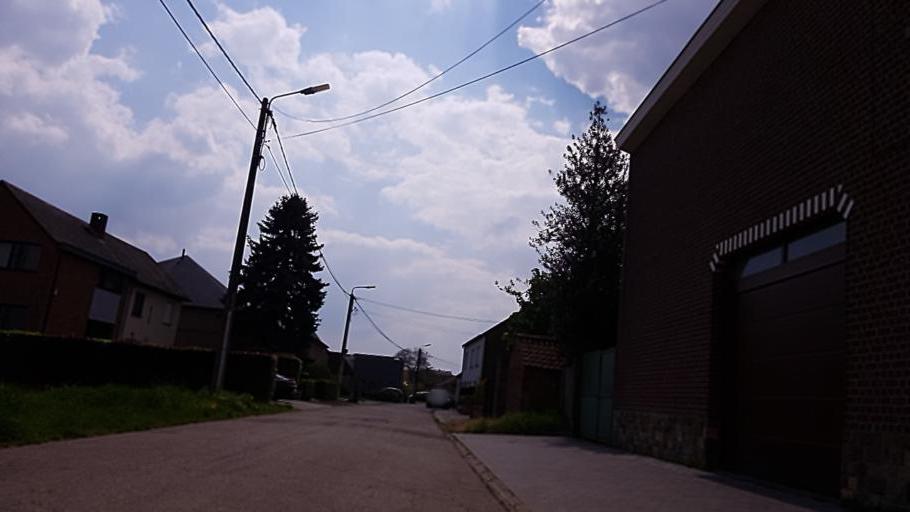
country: BE
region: Flanders
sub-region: Provincie Vlaams-Brabant
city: Kortenberg
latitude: 50.8608
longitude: 4.5634
